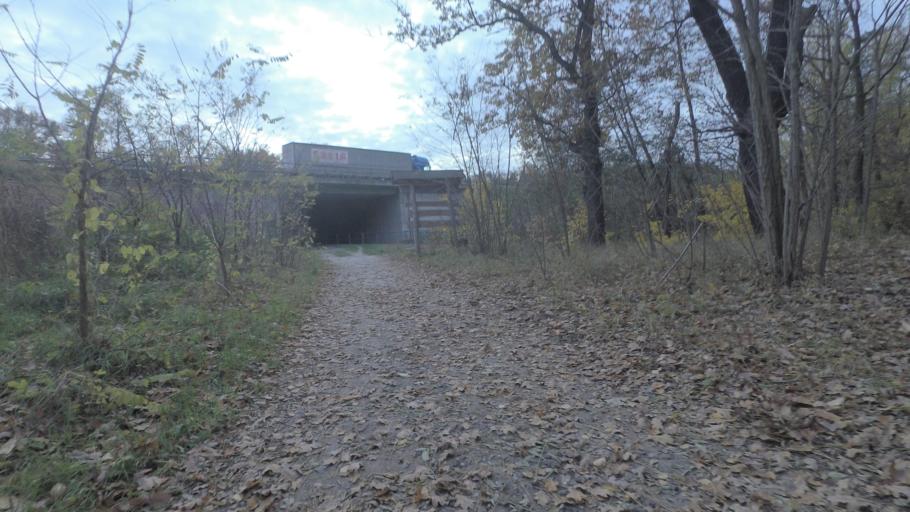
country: DE
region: Brandenburg
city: Rangsdorf
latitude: 52.3063
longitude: 13.4181
